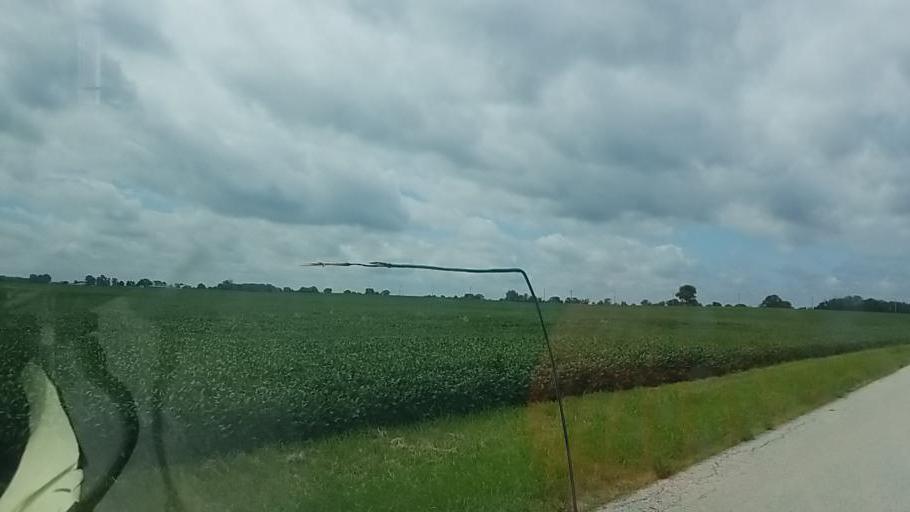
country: US
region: Ohio
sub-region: Fayette County
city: Jeffersonville
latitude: 39.7011
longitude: -83.5854
